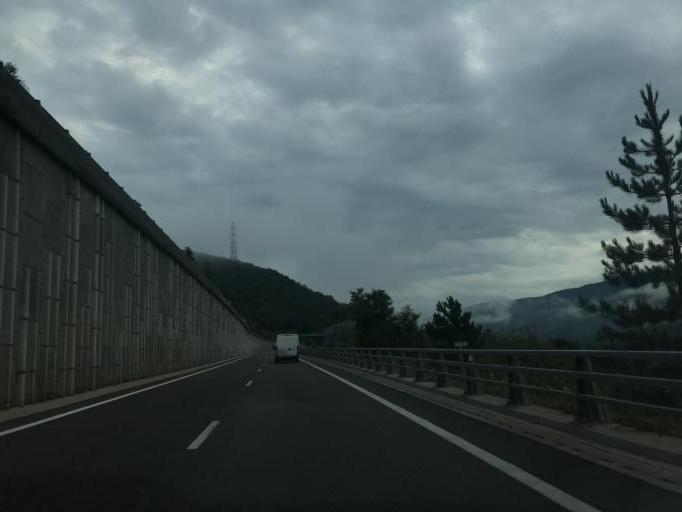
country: FR
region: Rhone-Alpes
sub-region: Departement de l'Ain
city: Montreal-la-Cluse
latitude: 46.1914
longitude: 5.5761
